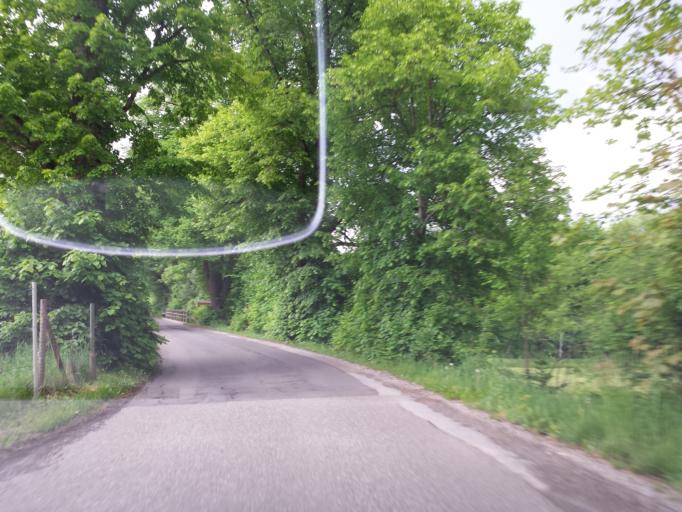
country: AT
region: Styria
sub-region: Politischer Bezirk Graz-Umgebung
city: Thal
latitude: 47.0567
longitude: 15.3653
